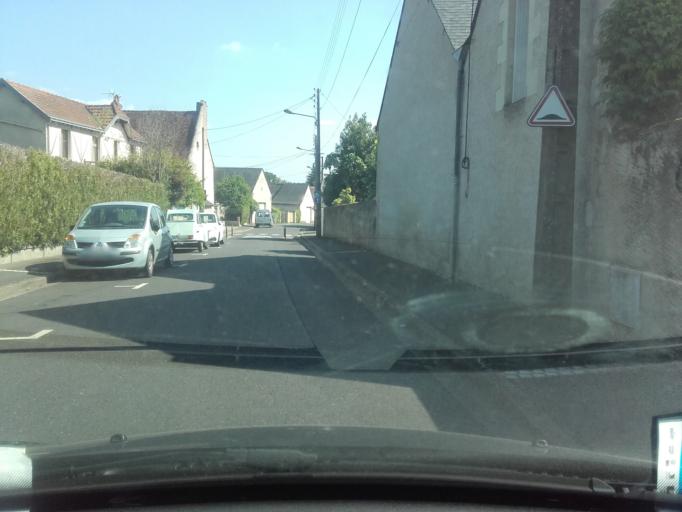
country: FR
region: Centre
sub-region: Departement d'Indre-et-Loire
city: Saint-Cyr-sur-Loire
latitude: 47.4093
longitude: 0.6710
